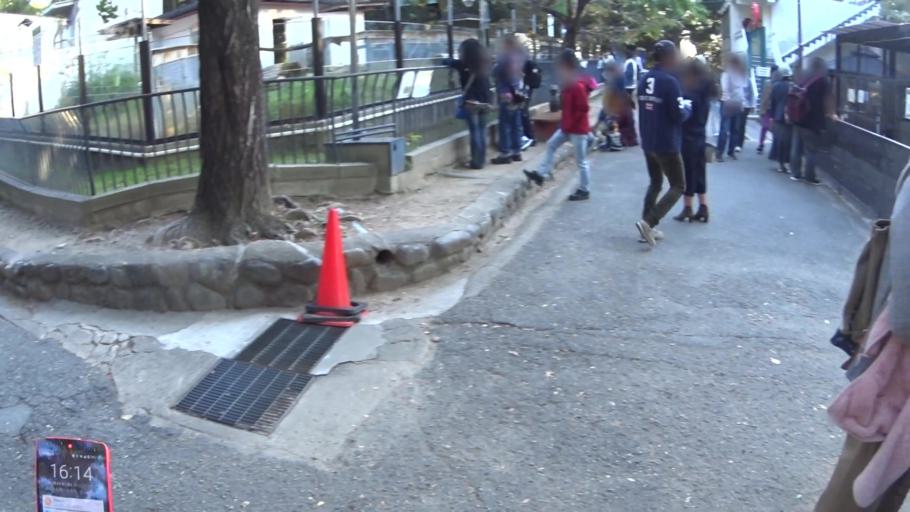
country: JP
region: Osaka
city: Ikeda
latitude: 34.8307
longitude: 135.4250
